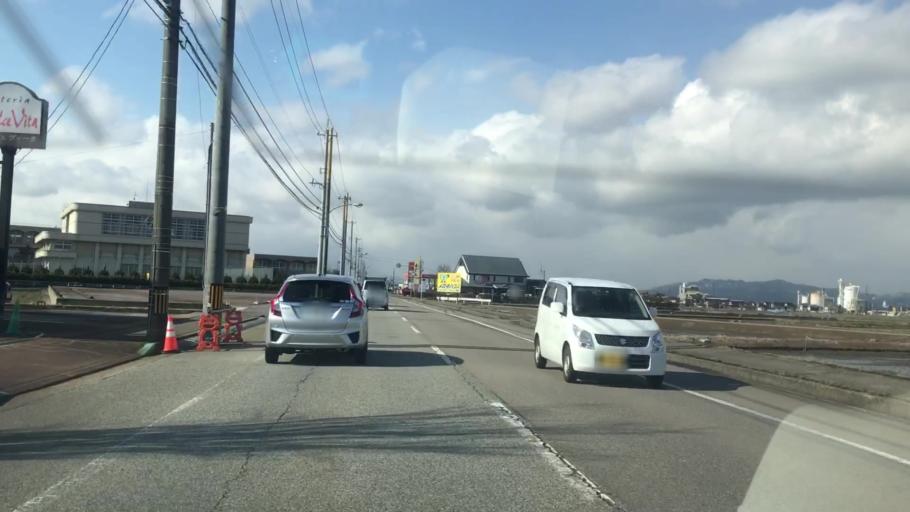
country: JP
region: Toyama
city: Nishishinminato
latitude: 36.7248
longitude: 137.0663
